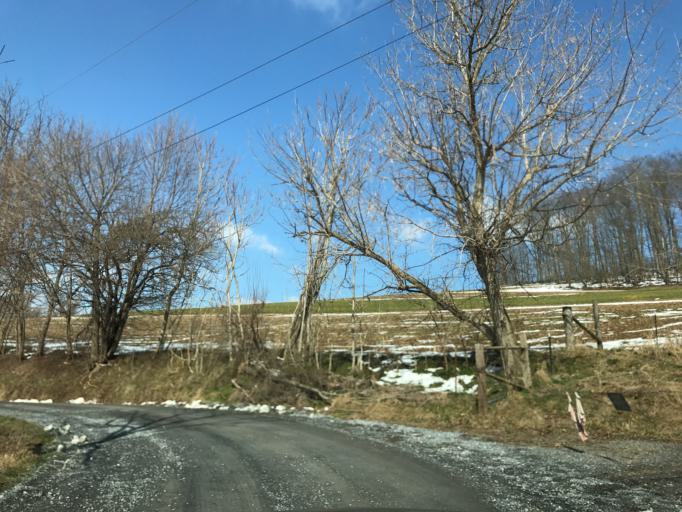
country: US
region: Maryland
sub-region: Carroll County
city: Manchester
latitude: 39.6899
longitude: -76.8211
